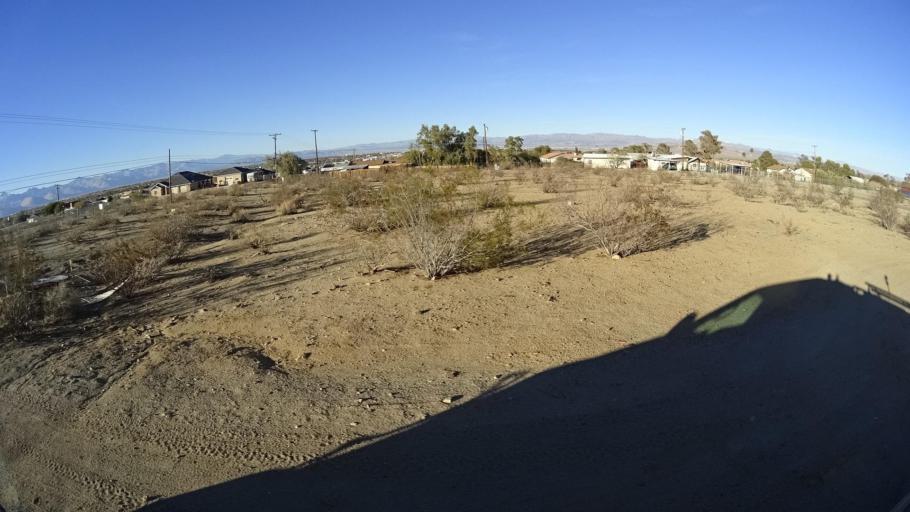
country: US
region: California
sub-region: Kern County
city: Ridgecrest
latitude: 35.5862
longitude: -117.6652
